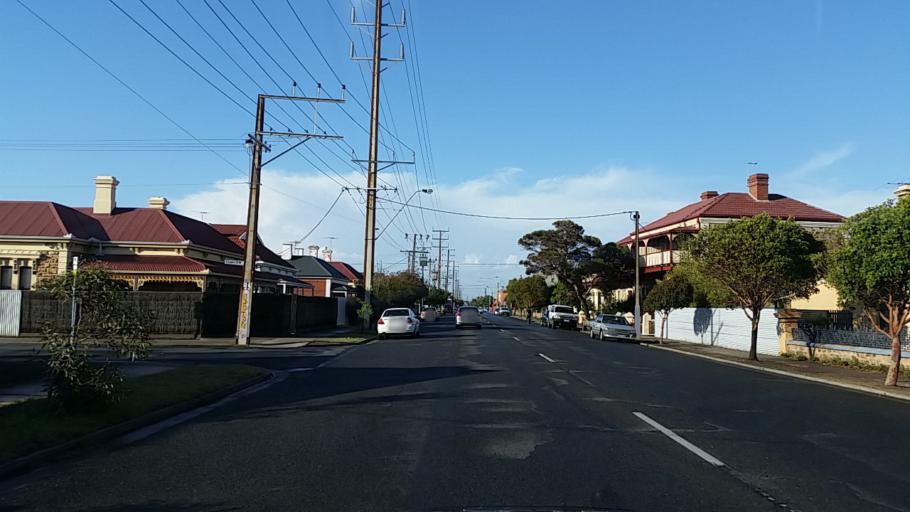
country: AU
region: South Australia
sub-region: Port Adelaide Enfield
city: Birkenhead
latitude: -34.8413
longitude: 138.4830
